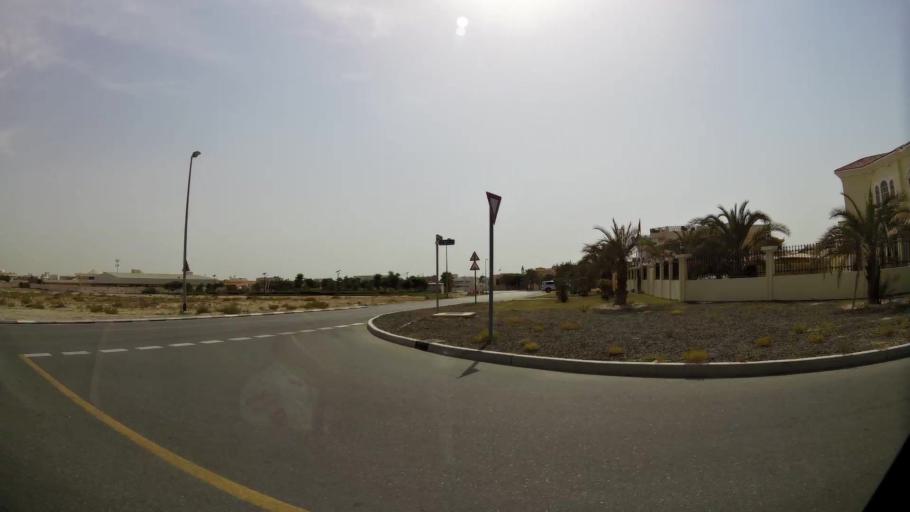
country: AE
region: Ash Shariqah
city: Sharjah
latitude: 25.2527
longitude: 55.4372
